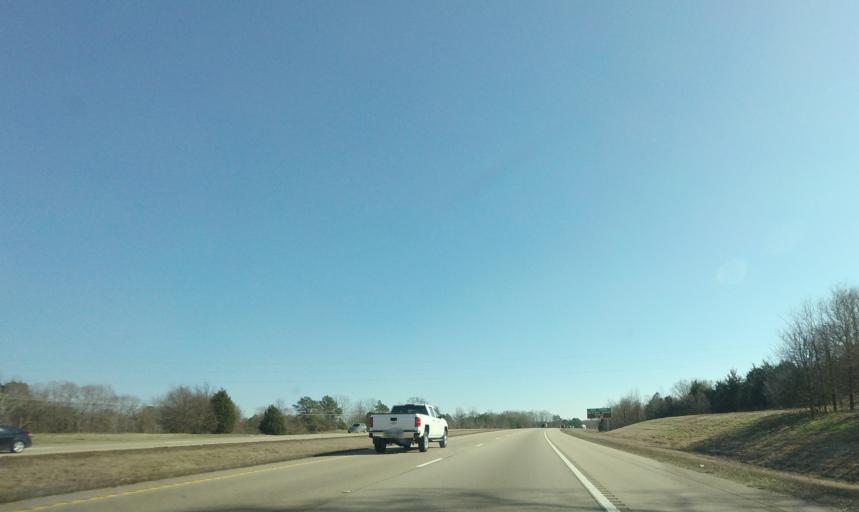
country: US
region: Mississippi
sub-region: Marshall County
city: Holly Springs
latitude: 34.8036
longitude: -89.5029
